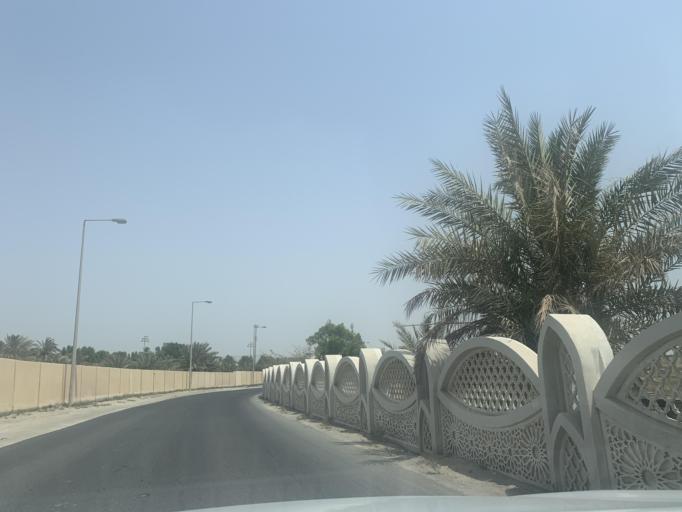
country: BH
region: Manama
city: Jidd Hafs
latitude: 26.2269
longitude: 50.4645
